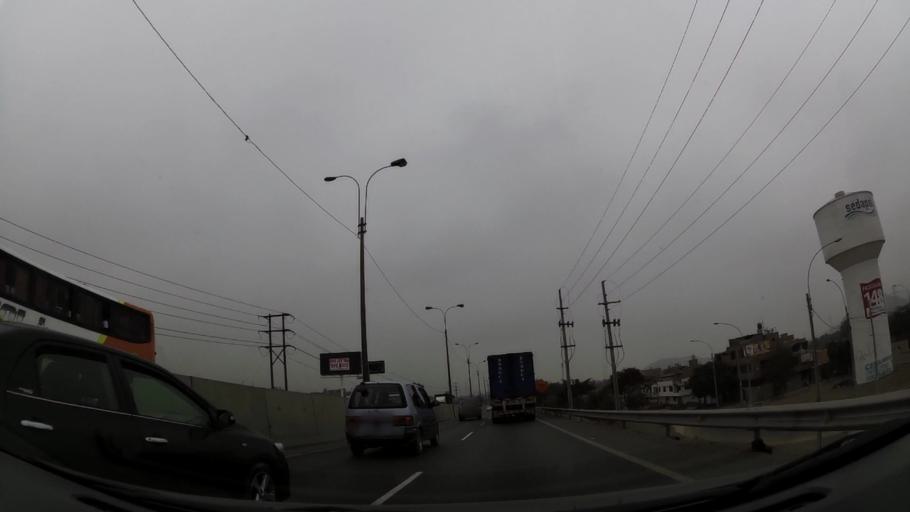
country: PE
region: Lima
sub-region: Lima
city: Urb. Santo Domingo
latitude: -11.9186
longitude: -77.0736
